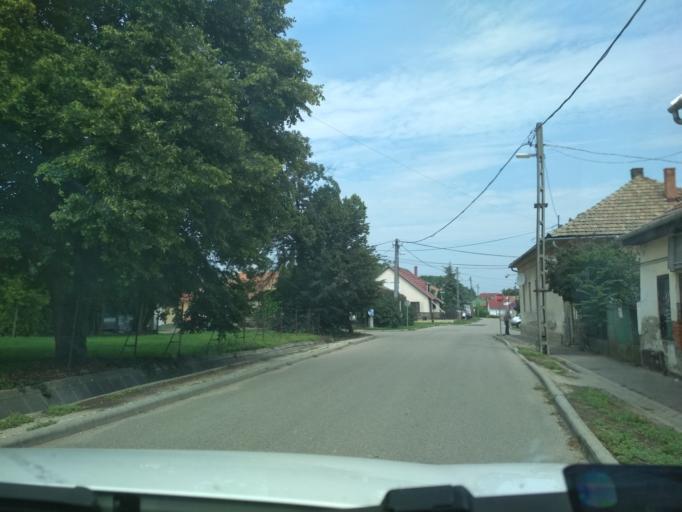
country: HU
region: Jasz-Nagykun-Szolnok
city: Tiszafured
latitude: 47.6174
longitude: 20.7592
